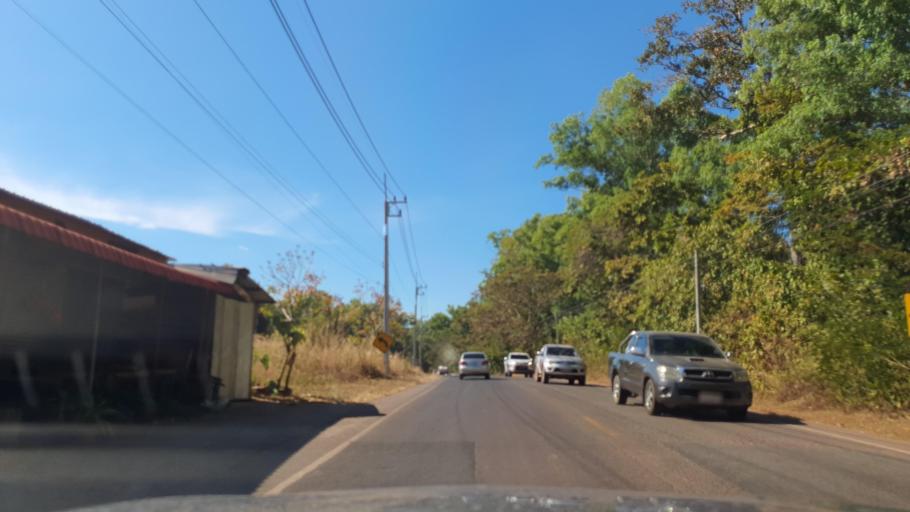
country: TH
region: Kalasin
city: Khao Wong
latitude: 16.7632
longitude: 104.1476
